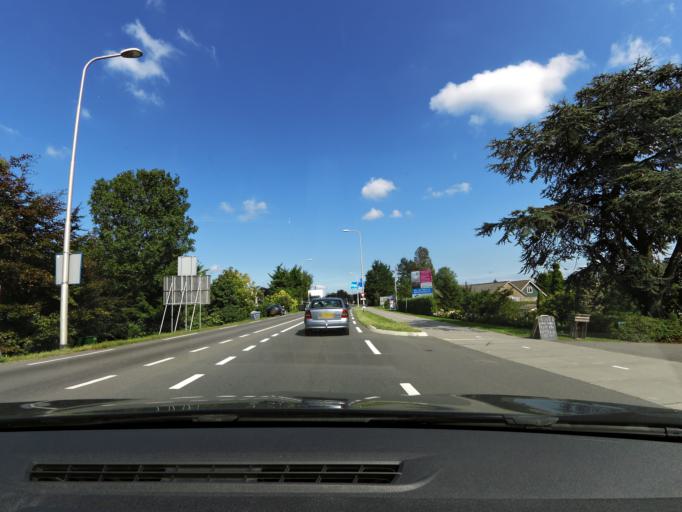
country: NL
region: North Holland
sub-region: Gemeente Aalsmeer
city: Aalsmeer
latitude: 52.2628
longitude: 4.7975
